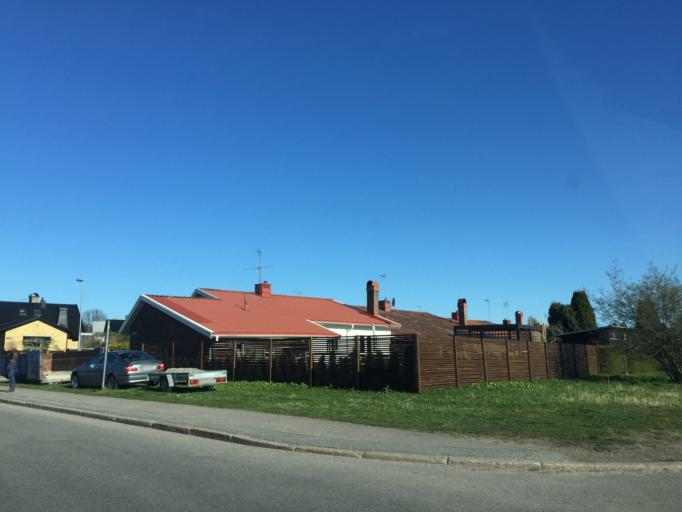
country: SE
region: OErebro
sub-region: Orebro Kommun
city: Orebro
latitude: 59.2626
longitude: 15.2138
